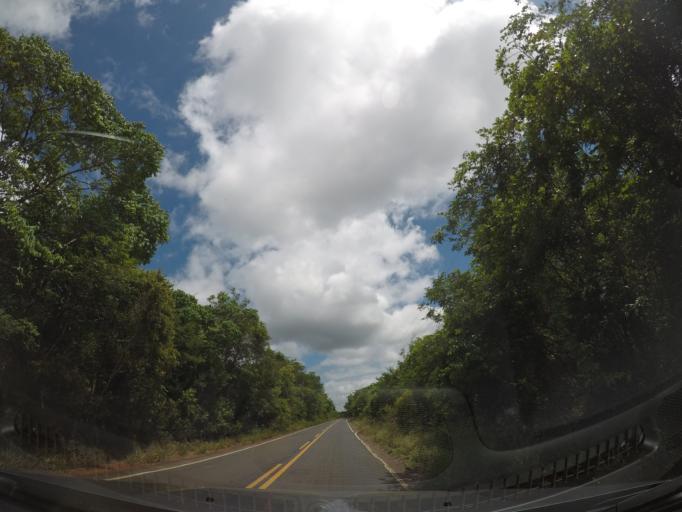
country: BR
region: Bahia
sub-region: Andarai
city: Vera Cruz
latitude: -12.5168
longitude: -41.3626
